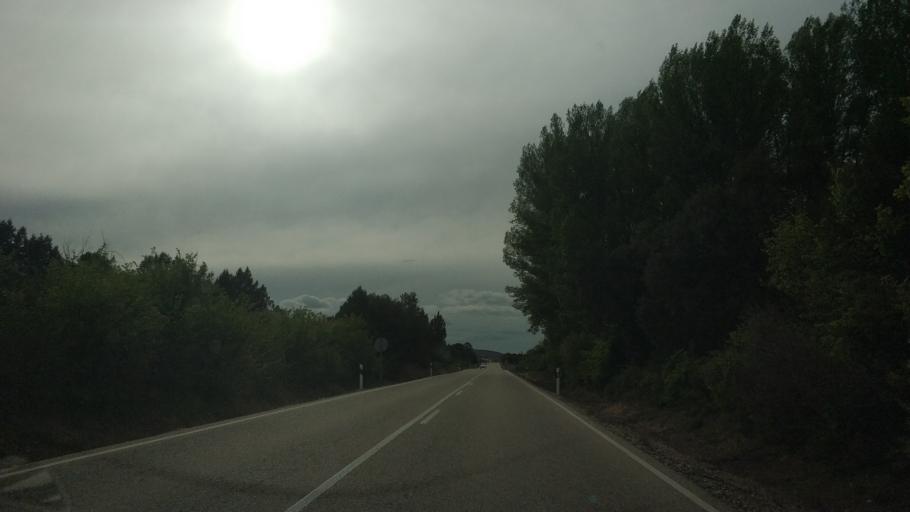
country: ES
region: Castille and Leon
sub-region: Provincia de Soria
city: Valdenebro
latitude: 41.5649
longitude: -2.9947
